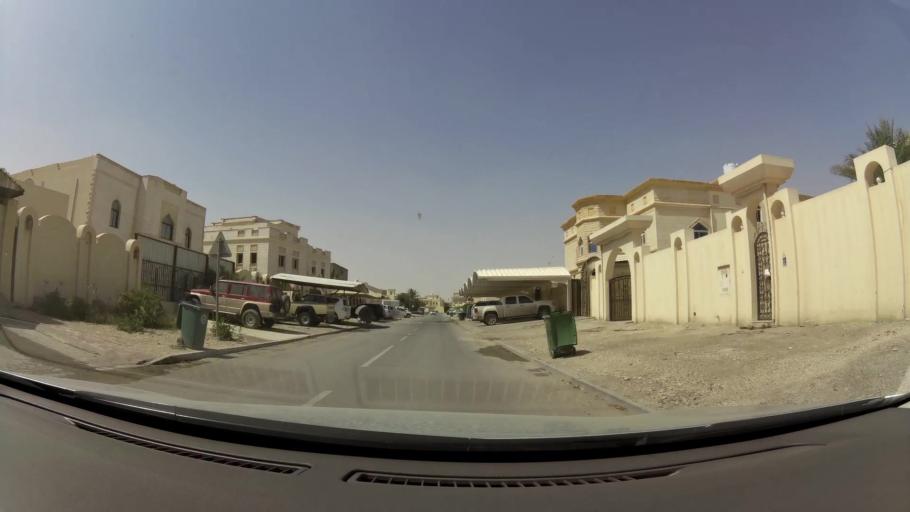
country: QA
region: Baladiyat Umm Salal
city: Umm Salal Muhammad
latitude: 25.3823
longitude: 51.4237
